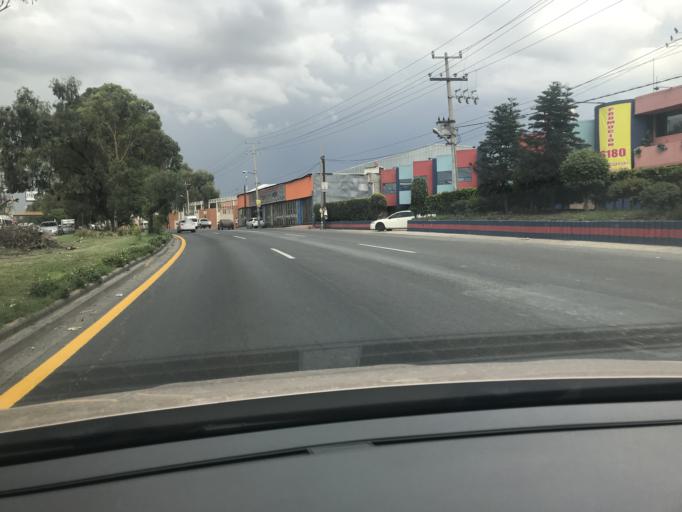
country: MX
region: Mexico
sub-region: La Paz
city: El Pino
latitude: 19.3555
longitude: -98.9576
